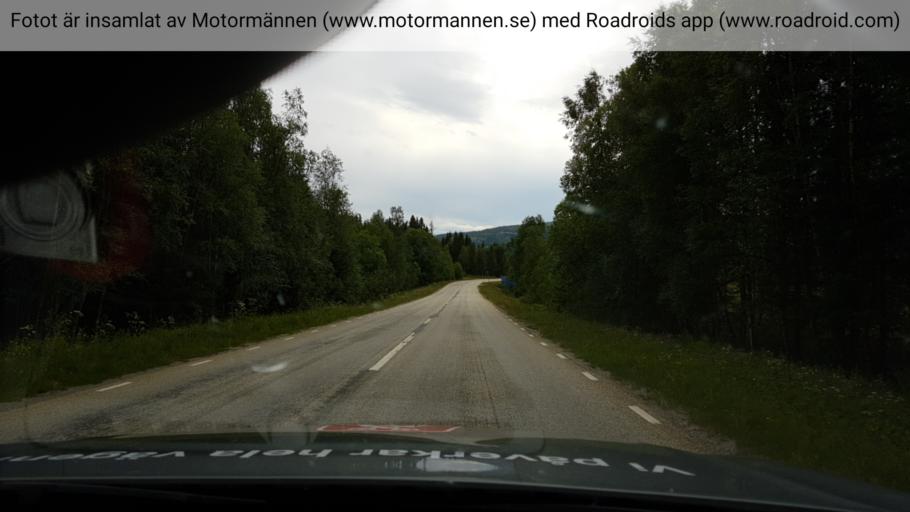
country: SE
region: Jaemtland
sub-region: Bergs Kommun
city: Hoverberg
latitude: 62.5345
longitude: 14.2105
